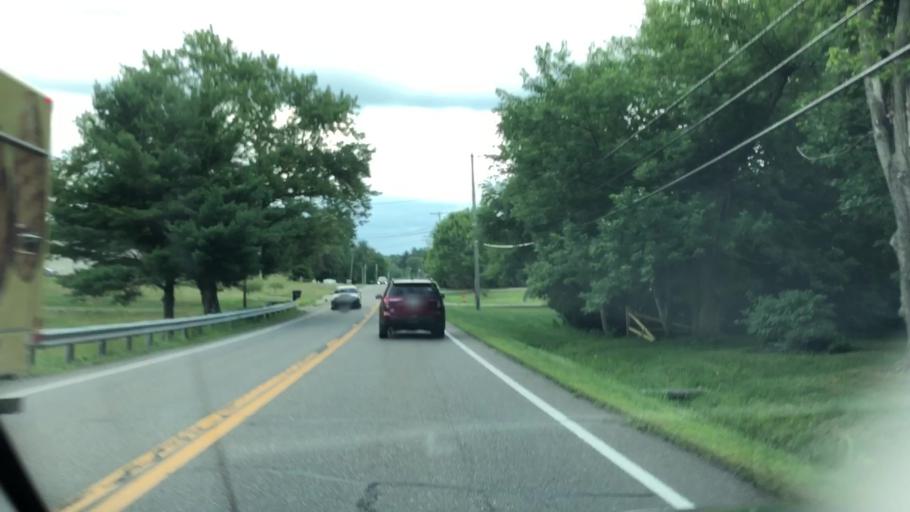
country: US
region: Ohio
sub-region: Summit County
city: Green
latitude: 40.9442
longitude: -81.4883
